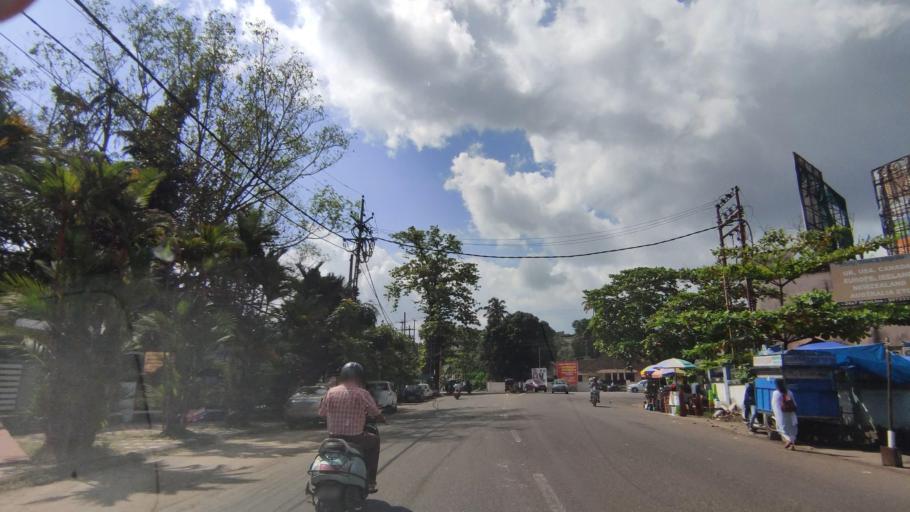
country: IN
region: Kerala
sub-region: Kottayam
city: Kottayam
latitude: 9.5928
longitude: 76.5281
